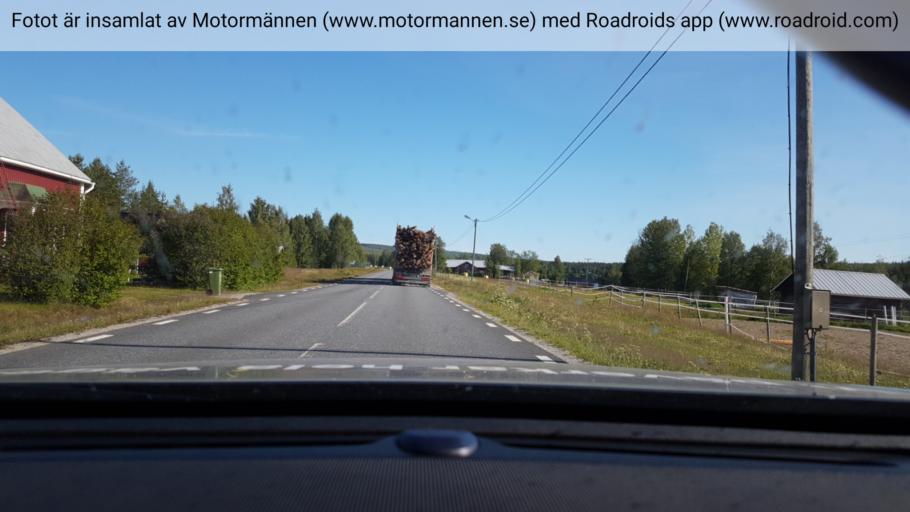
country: SE
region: Vaesterbotten
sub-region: Bjurholms Kommun
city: Bjurholm
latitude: 64.3072
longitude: 19.1635
